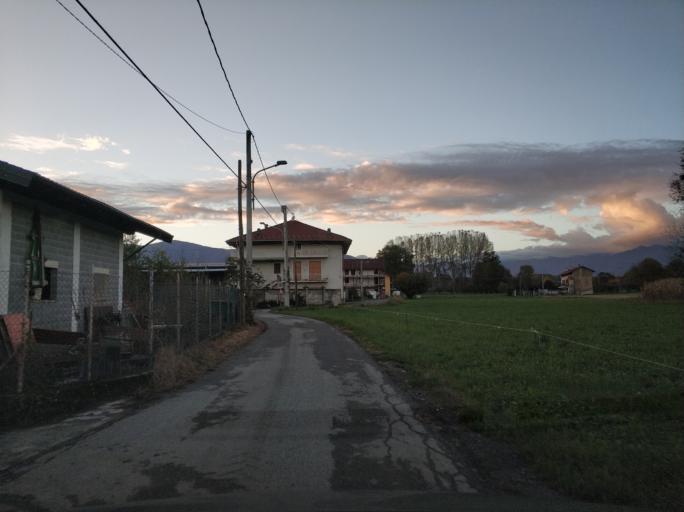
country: IT
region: Piedmont
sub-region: Provincia di Torino
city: Robassomero
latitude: 45.2144
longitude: 7.5779
